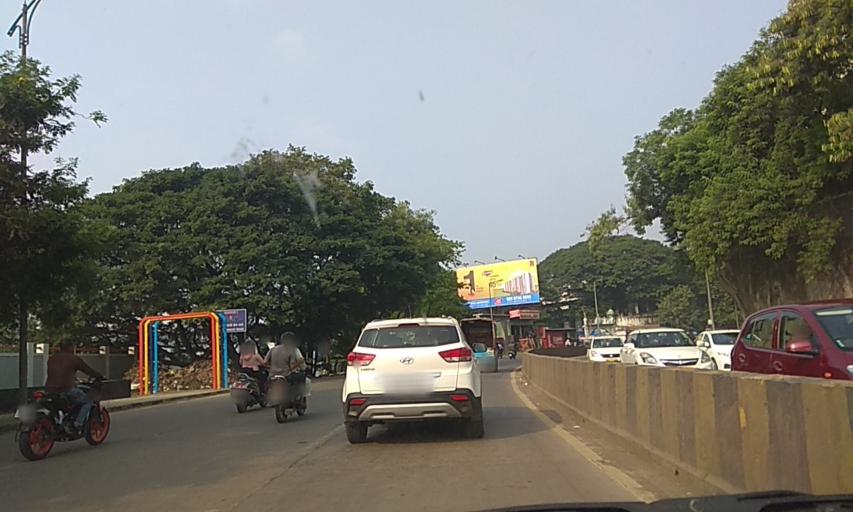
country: IN
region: Maharashtra
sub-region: Pune Division
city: Shivaji Nagar
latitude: 18.5438
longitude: 73.8797
